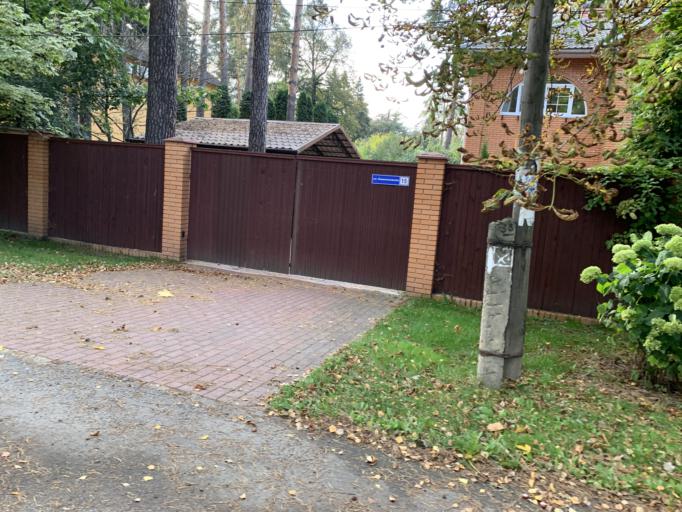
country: RU
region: Moskovskaya
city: Mamontovka
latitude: 55.9854
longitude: 37.8314
